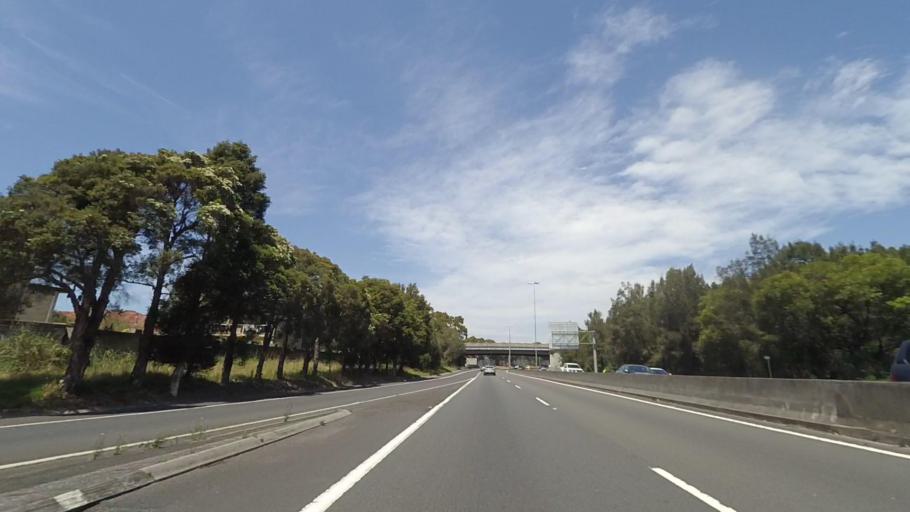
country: AU
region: New South Wales
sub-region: Wollongong
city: Gwynneville
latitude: -34.4118
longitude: 150.8829
